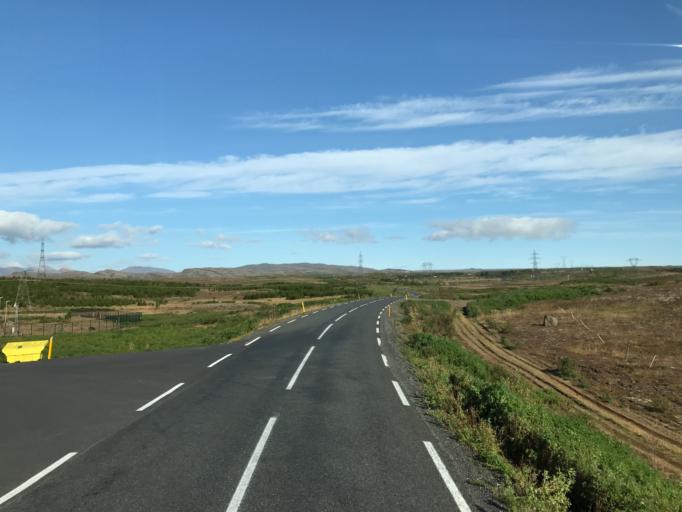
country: IS
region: Capital Region
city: Mosfellsbaer
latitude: 64.0981
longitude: -21.6963
